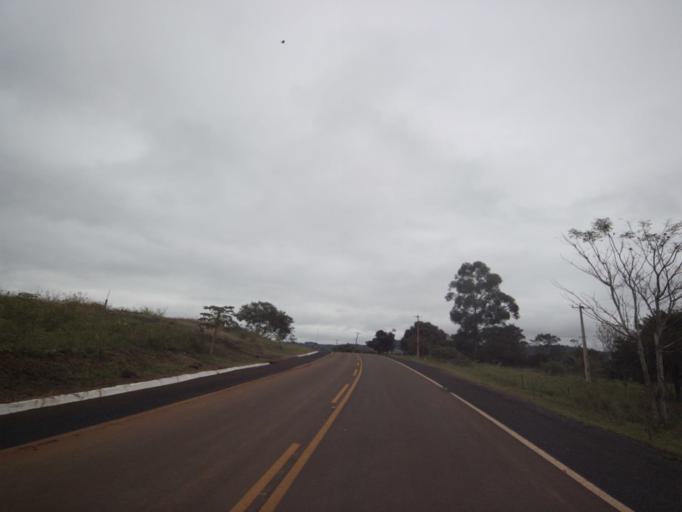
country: AR
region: Misiones
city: El Soberbio
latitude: -27.2876
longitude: -54.1876
